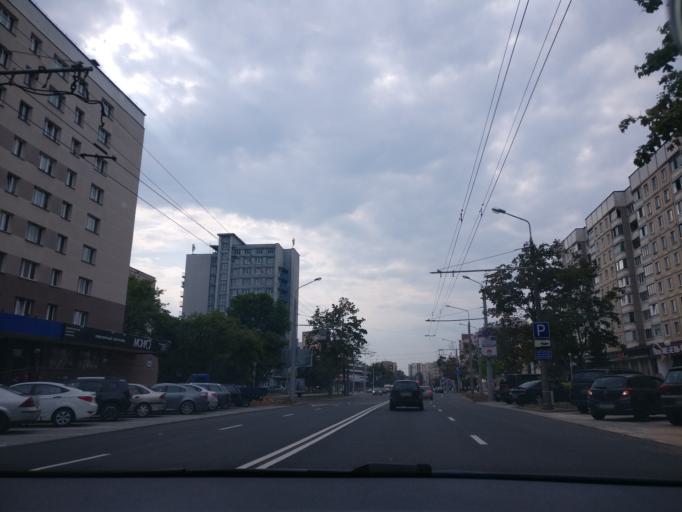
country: BY
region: Minsk
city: Minsk
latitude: 53.9235
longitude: 27.5799
